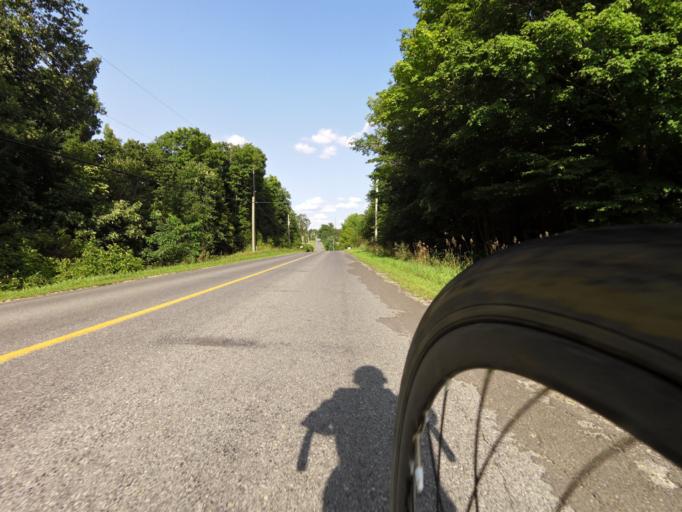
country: CA
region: Ontario
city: Kingston
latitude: 44.3622
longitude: -76.6325
